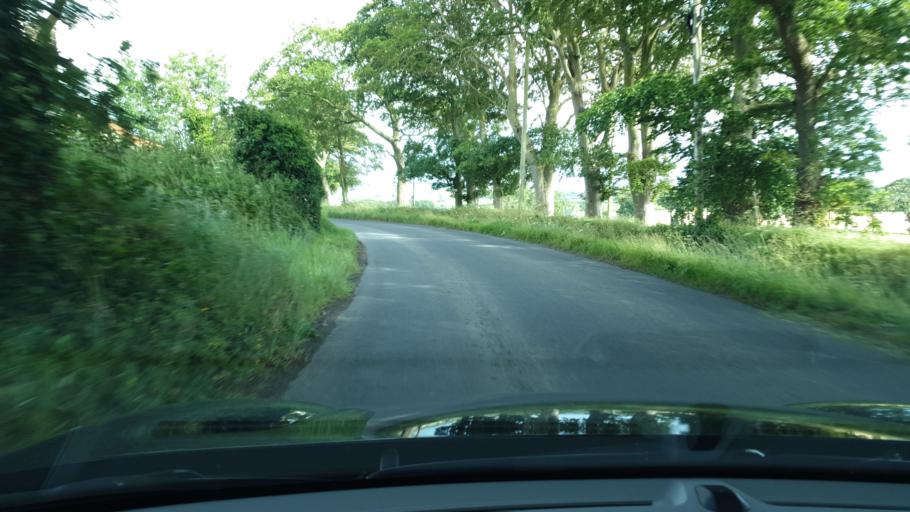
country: IE
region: Leinster
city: Balrothery
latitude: 53.5611
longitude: -6.1810
